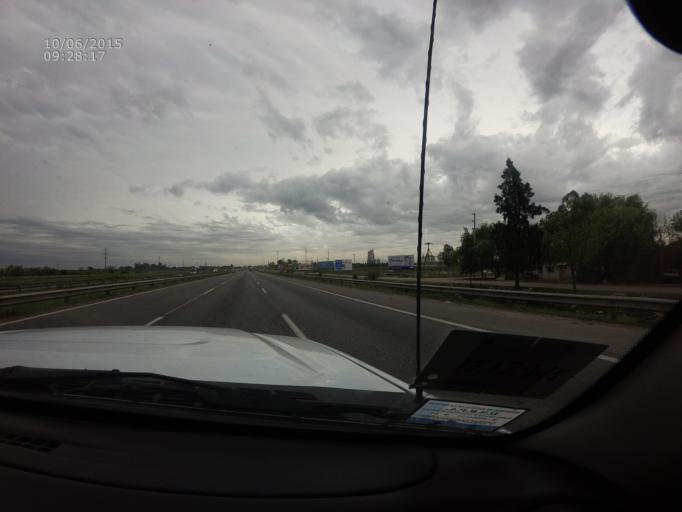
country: AR
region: Buenos Aires
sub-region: Partido de Campana
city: Campana
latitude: -34.1609
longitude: -59.0094
